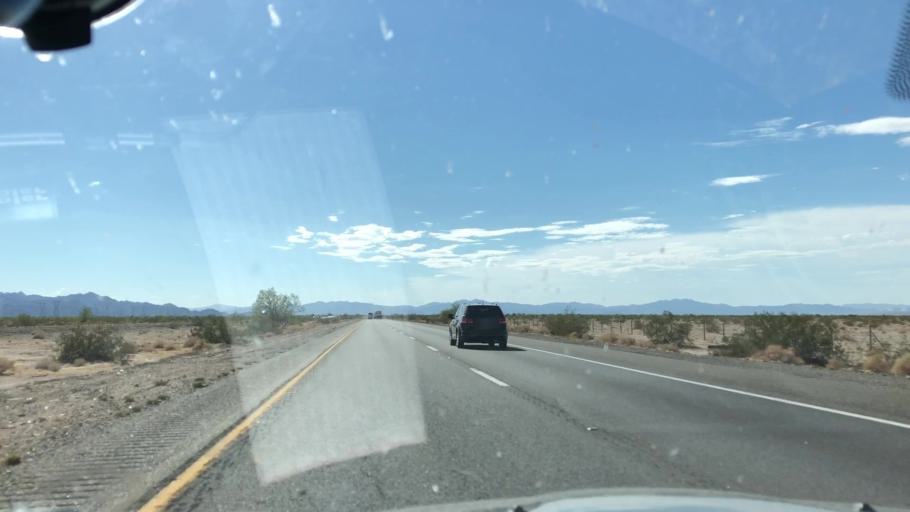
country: US
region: California
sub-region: Riverside County
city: Mesa Verde
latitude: 33.6673
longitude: -115.1919
